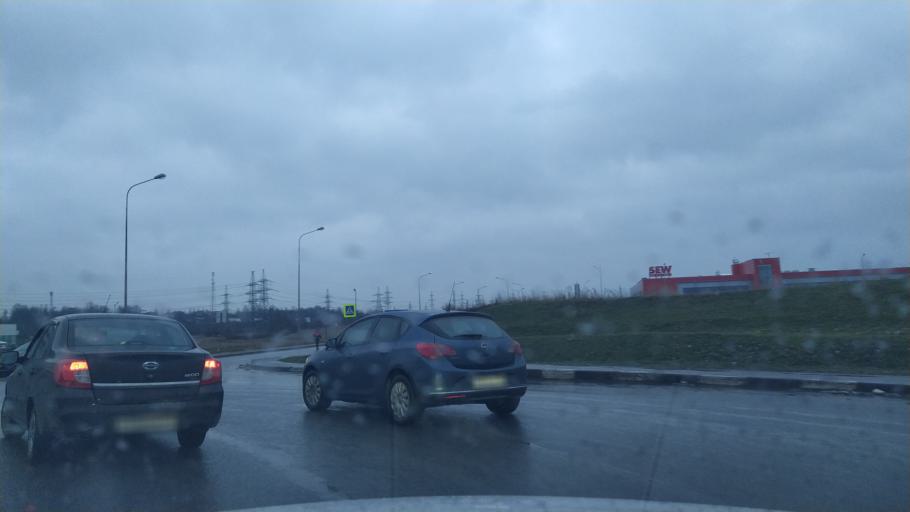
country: RU
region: Leningrad
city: Bugry
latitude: 60.0950
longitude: 30.3835
